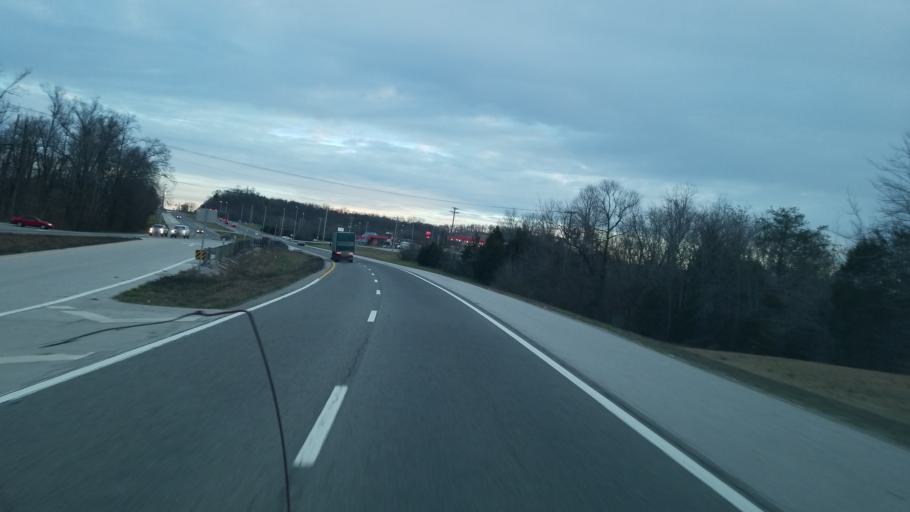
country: US
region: Tennessee
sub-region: Putnam County
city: Cookeville
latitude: 36.1283
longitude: -85.4817
